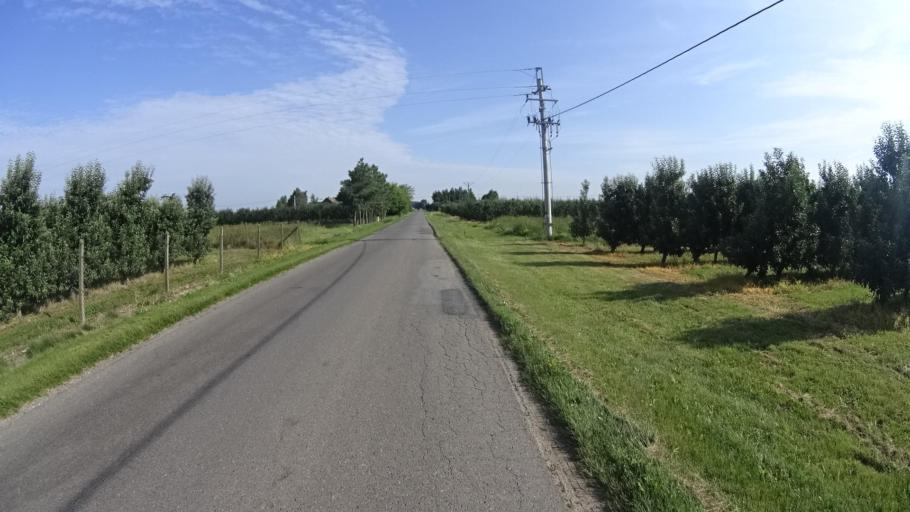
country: PL
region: Masovian Voivodeship
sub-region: Powiat grojecki
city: Goszczyn
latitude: 51.7606
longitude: 20.8531
